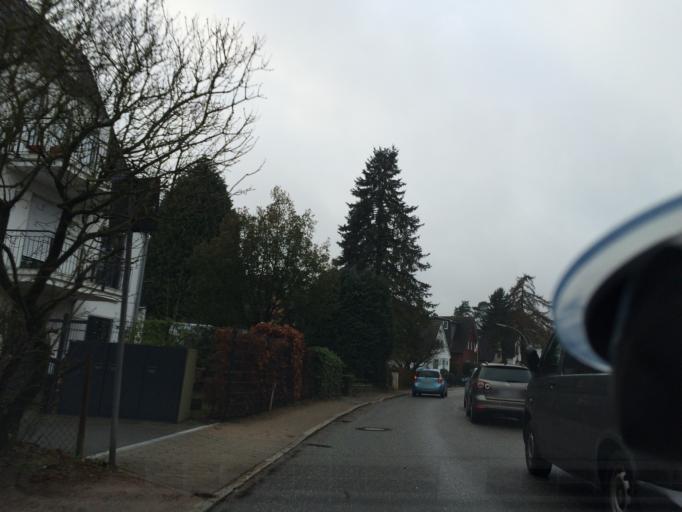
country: DE
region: Schleswig-Holstein
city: Halstenbek
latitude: 53.5684
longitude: 9.8255
